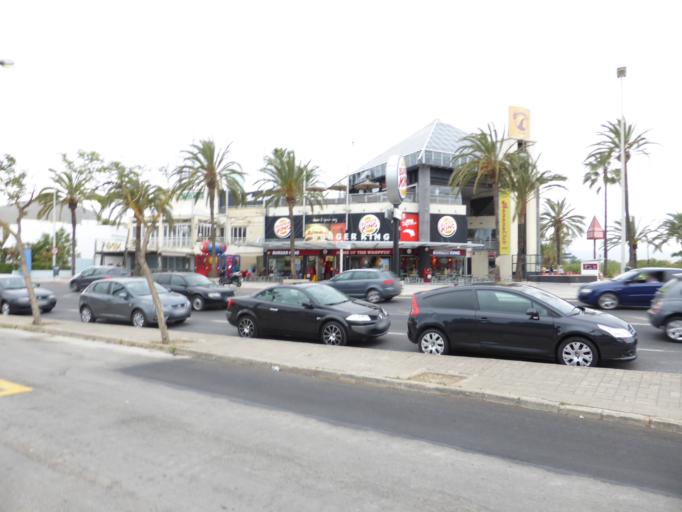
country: ES
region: Balearic Islands
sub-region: Illes Balears
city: Port d'Alcudia
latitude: 39.8402
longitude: 3.1225
